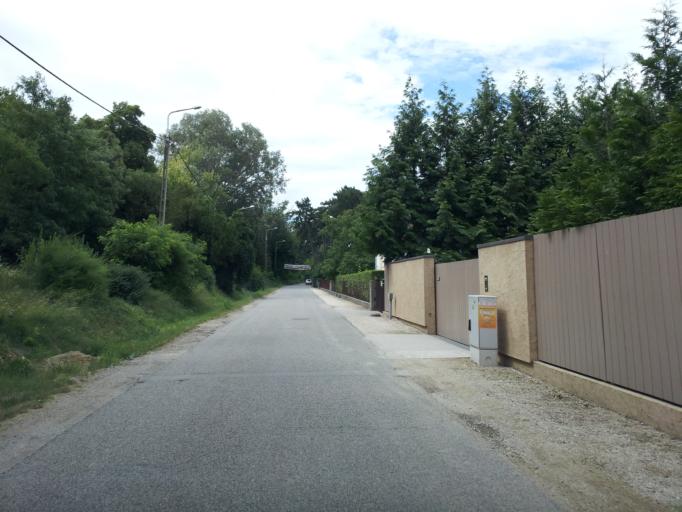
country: HU
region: Somogy
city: Balatonszabadi
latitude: 46.9564
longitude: 18.1506
